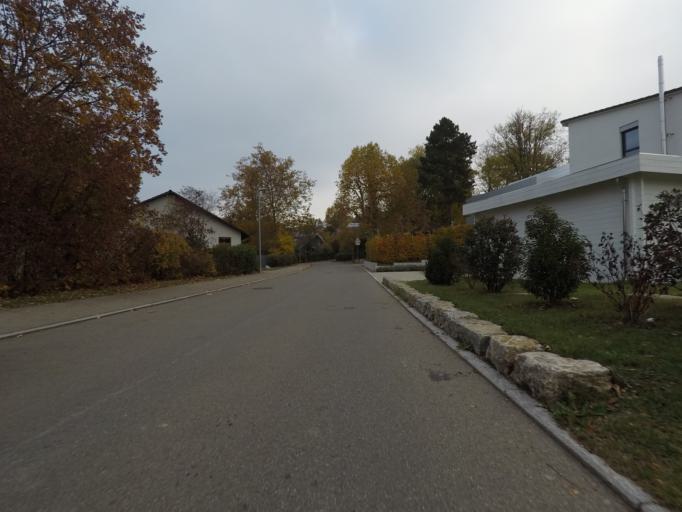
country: DE
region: Baden-Wuerttemberg
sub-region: Tuebingen Region
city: Pfullingen
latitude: 48.4886
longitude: 9.2301
